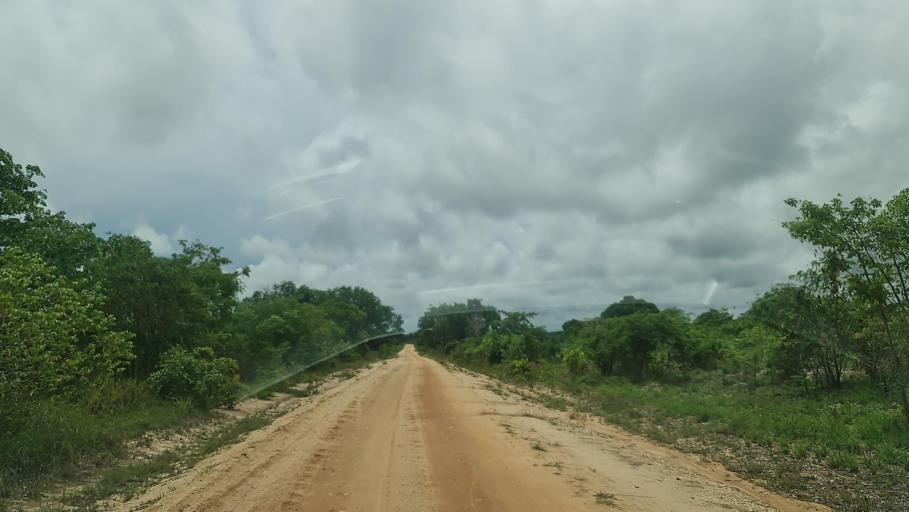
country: MZ
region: Zambezia
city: Quelimane
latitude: -17.2626
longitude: 37.2362
